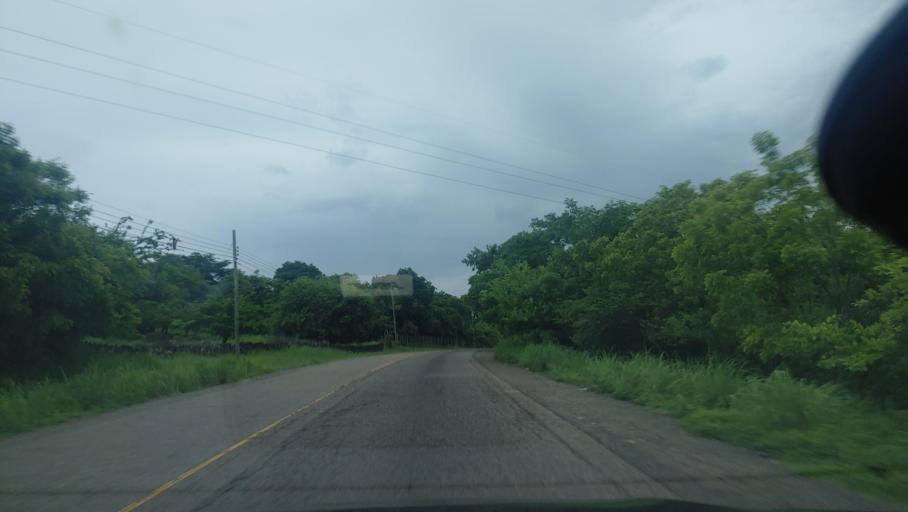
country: HN
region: Choluteca
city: Corpus
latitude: 13.3747
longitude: -87.0560
